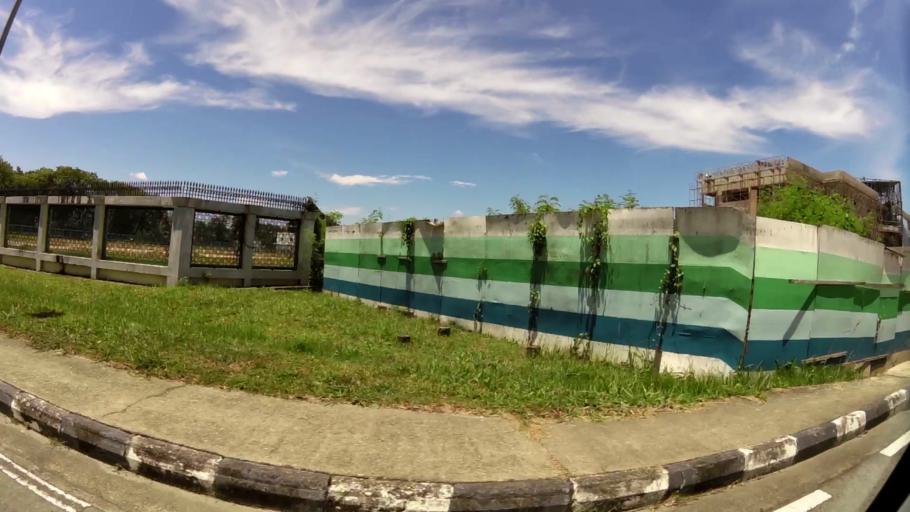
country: BN
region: Brunei and Muara
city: Bandar Seri Begawan
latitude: 4.9351
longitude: 114.9400
